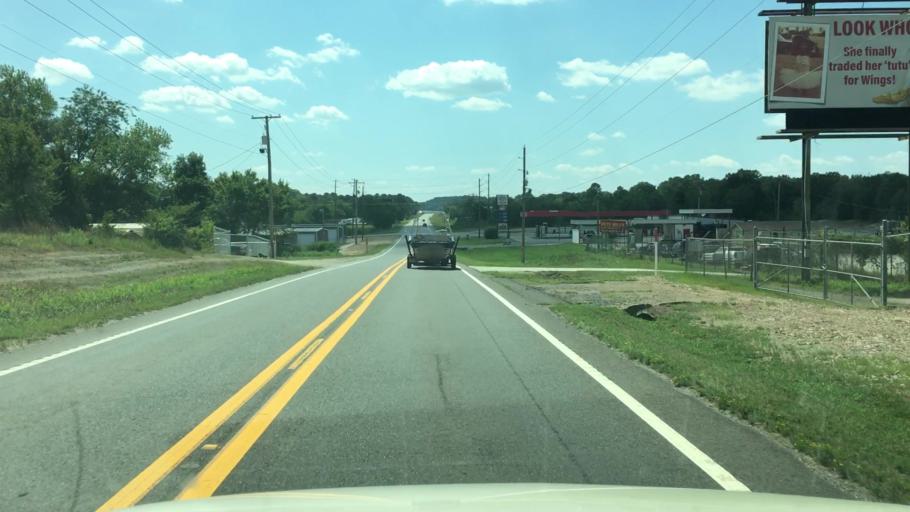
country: US
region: Arkansas
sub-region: Garland County
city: Piney
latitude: 34.5106
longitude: -93.2162
